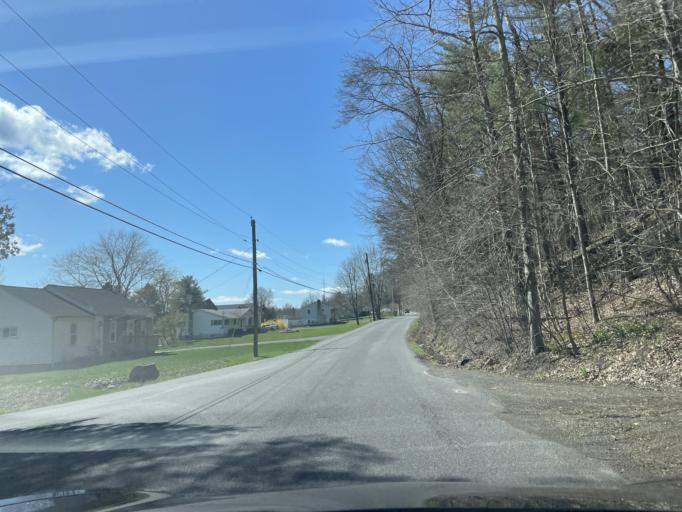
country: US
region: New York
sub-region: Ulster County
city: Saugerties South
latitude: 42.0605
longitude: -73.9883
